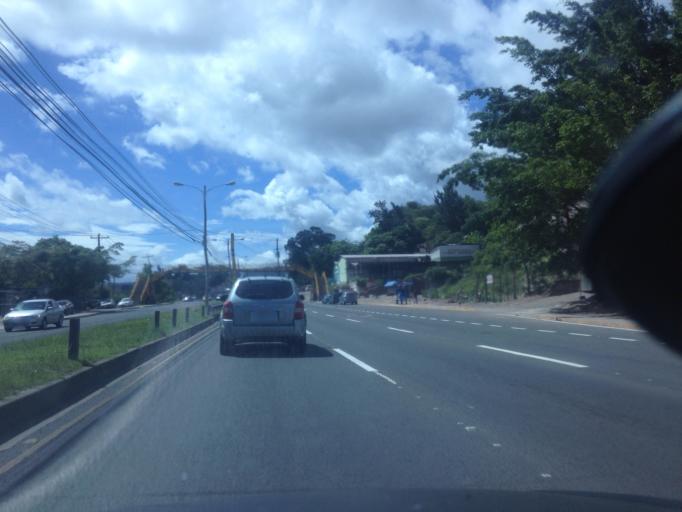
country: HN
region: Francisco Morazan
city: El Tablon
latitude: 14.0739
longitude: -87.1662
